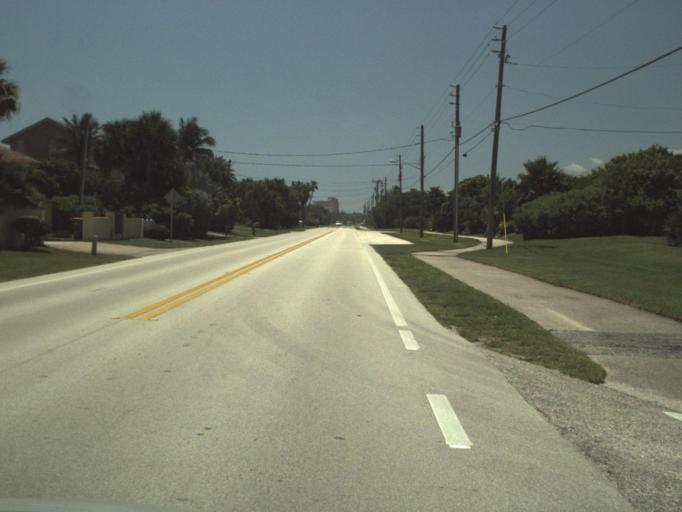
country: US
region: Florida
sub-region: Brevard County
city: Malabar
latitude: 27.9789
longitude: -80.5142
